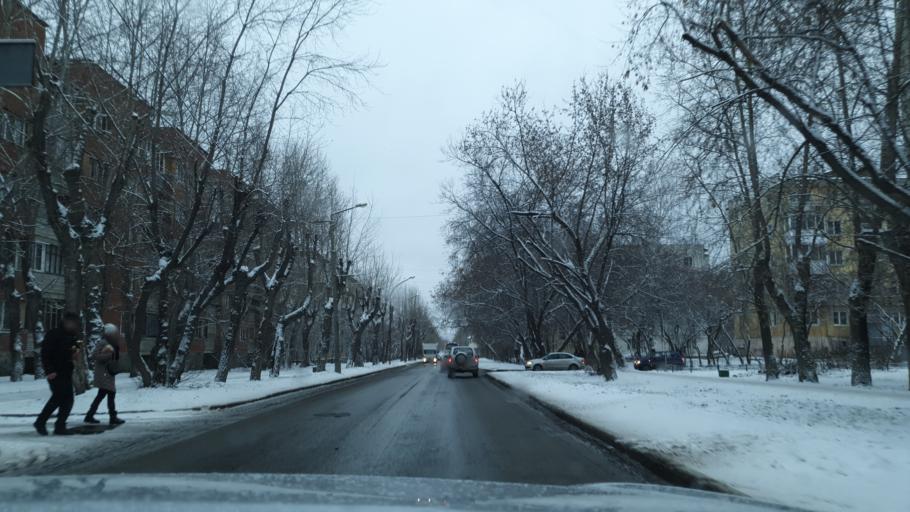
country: RU
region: Sverdlovsk
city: Istok
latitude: 56.7524
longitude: 60.7088
